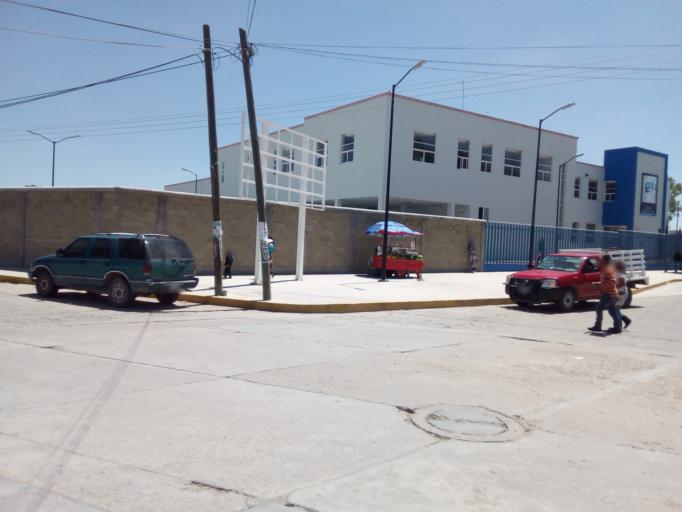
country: MX
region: Guerrero
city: San Luis de la Paz
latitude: 21.2933
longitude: -100.5272
